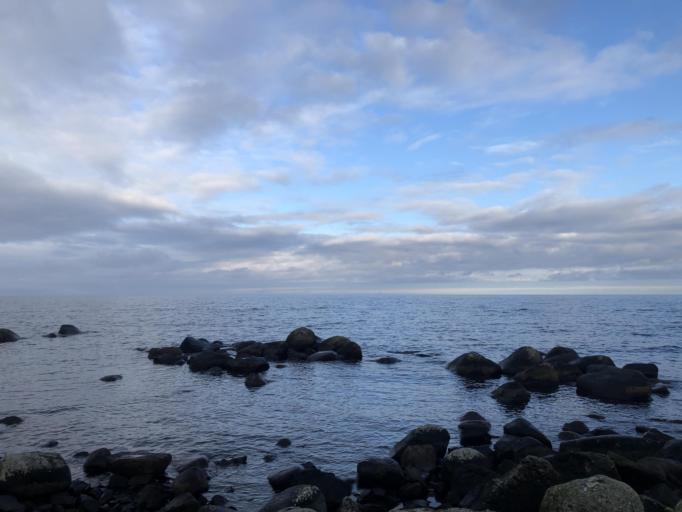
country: SE
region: Skane
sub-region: Simrishamns Kommun
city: Kivik
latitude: 55.6752
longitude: 14.2695
